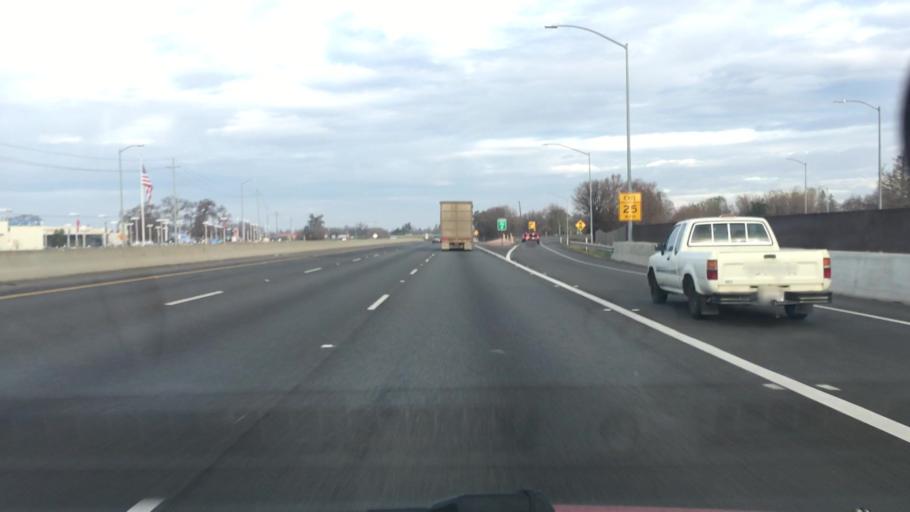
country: US
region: California
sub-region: Sacramento County
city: Elk Grove
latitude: 38.4048
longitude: -121.3858
